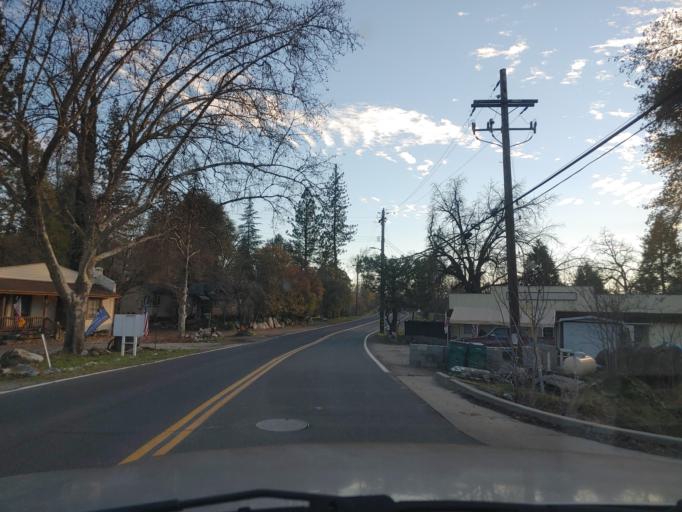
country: US
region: California
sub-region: Tuolumne County
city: Columbia
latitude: 38.0308
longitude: -120.4061
